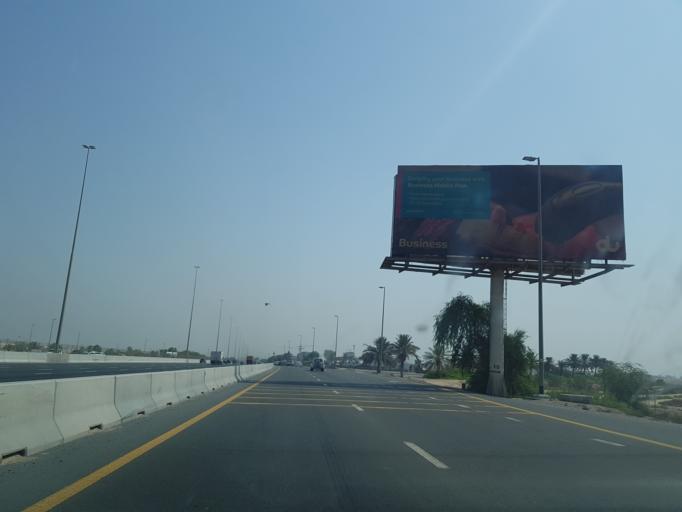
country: AE
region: Ash Shariqah
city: Sharjah
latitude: 25.1364
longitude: 55.3812
